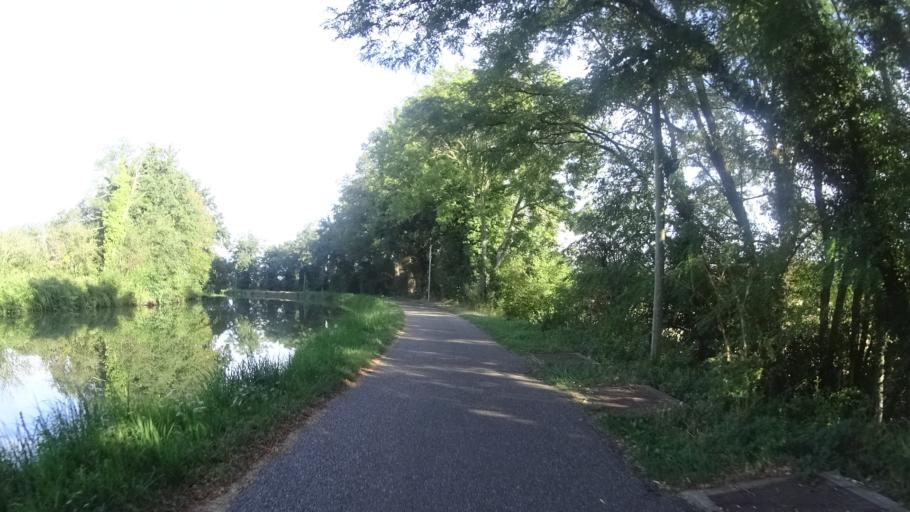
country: FR
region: Bourgogne
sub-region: Departement de Saone-et-Loire
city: Paray-le-Monial
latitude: 46.4787
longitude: 4.0661
